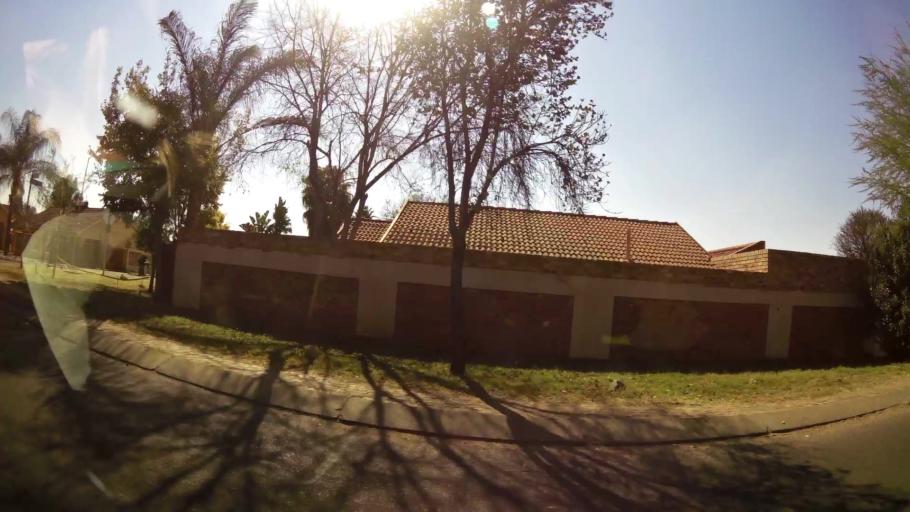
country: ZA
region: Gauteng
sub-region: City of Tshwane Metropolitan Municipality
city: Pretoria
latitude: -25.6569
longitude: 28.2598
